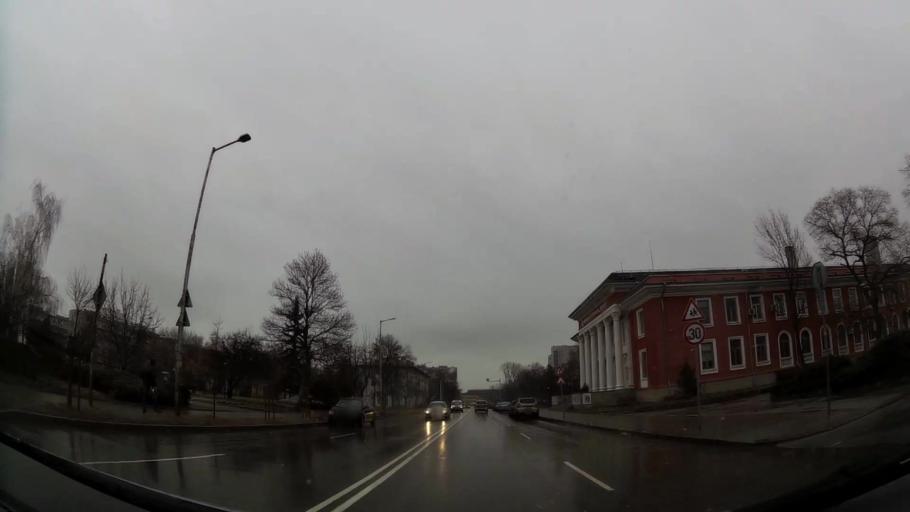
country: BG
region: Sofia-Capital
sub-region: Stolichna Obshtina
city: Sofia
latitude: 42.6654
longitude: 23.3998
